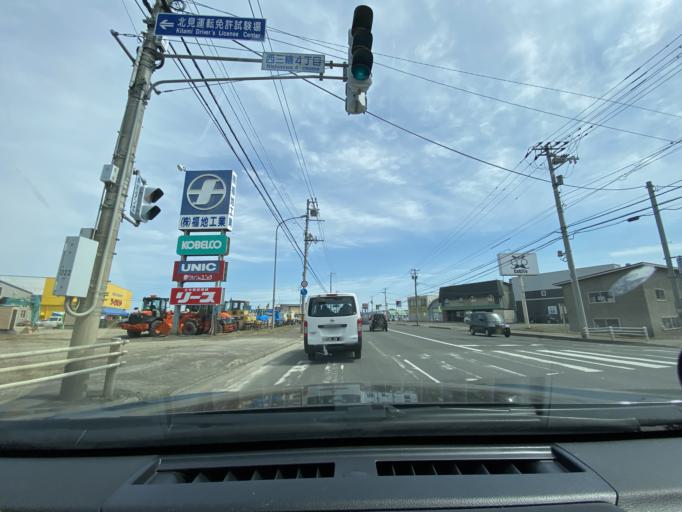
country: JP
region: Hokkaido
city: Kitami
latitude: 43.7994
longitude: 143.8291
